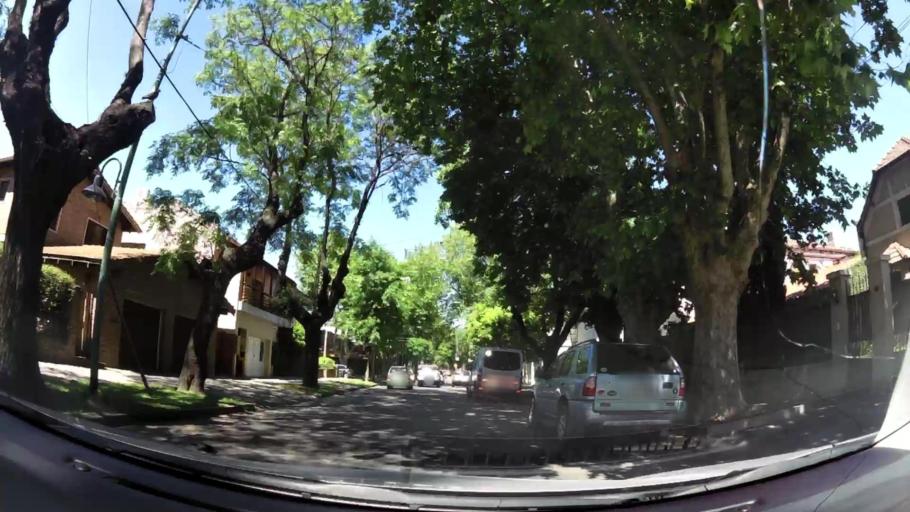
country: AR
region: Buenos Aires
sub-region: Partido de Vicente Lopez
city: Olivos
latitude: -34.5341
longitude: -58.4973
